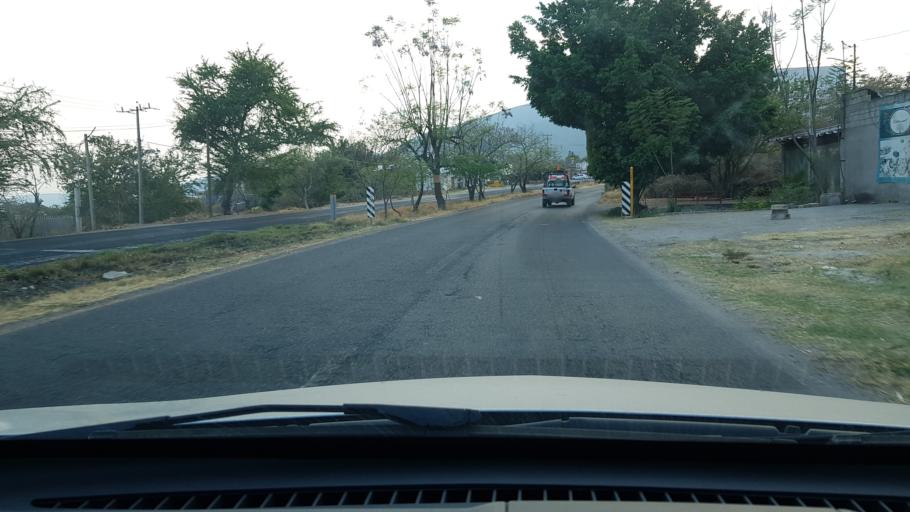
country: MX
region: Morelos
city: Yautepec
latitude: 18.8648
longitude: -99.0919
